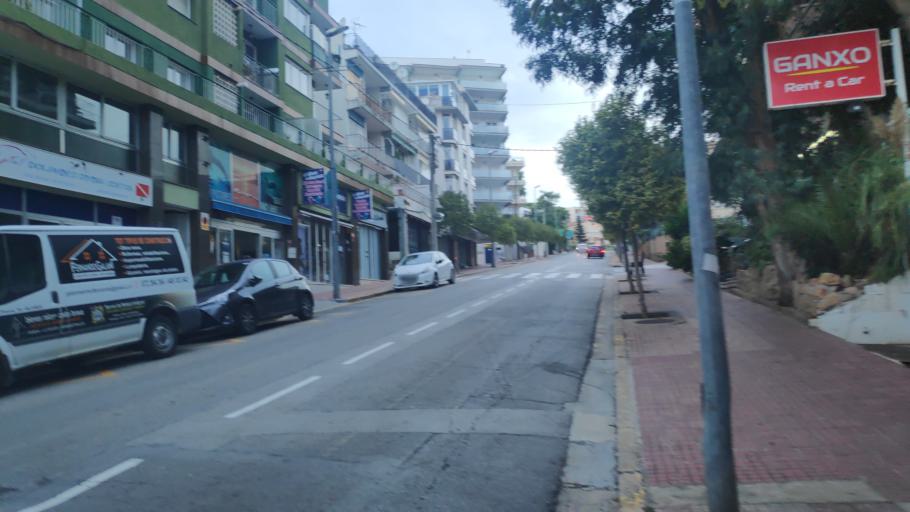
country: ES
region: Catalonia
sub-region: Provincia de Girona
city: Lloret de Mar
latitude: 41.7024
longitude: 2.8553
